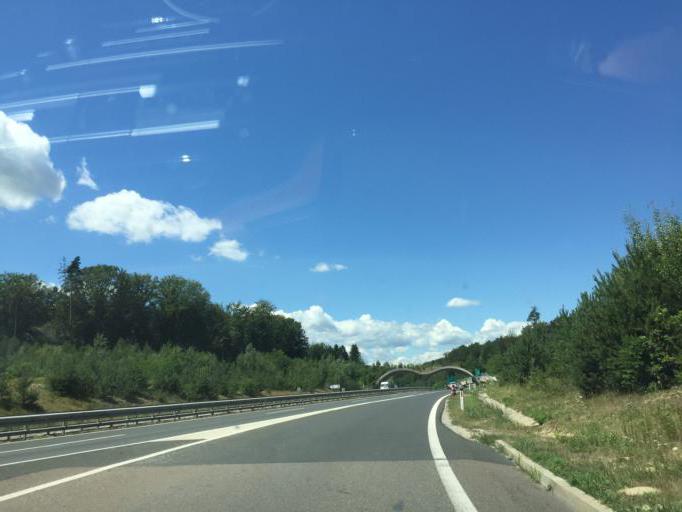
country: SI
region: Lenart
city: Lenart v Slov. Goricah
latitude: 46.5759
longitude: 15.8112
